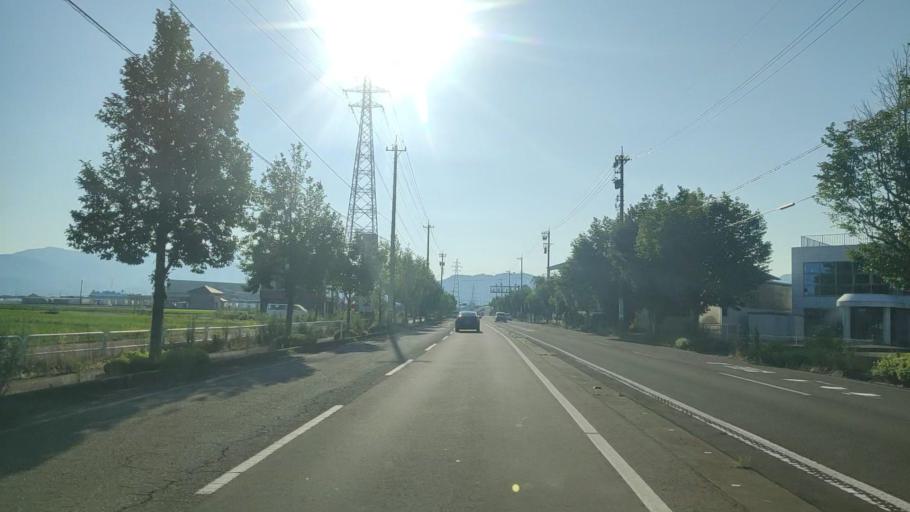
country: JP
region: Fukui
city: Fukui-shi
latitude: 36.0860
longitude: 136.2597
